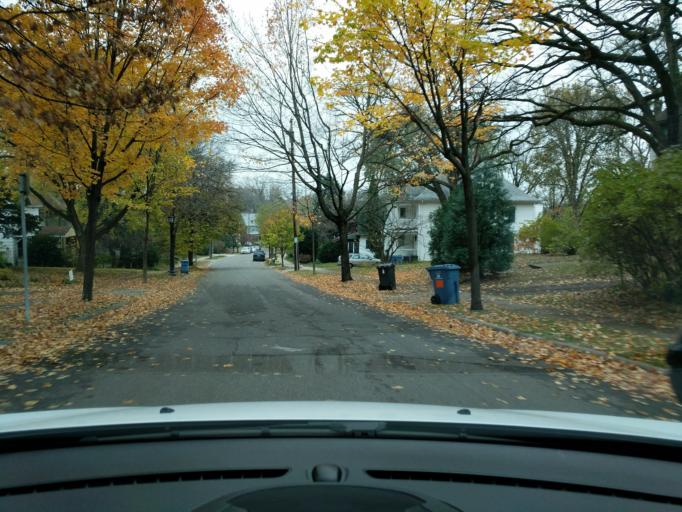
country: US
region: Minnesota
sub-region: Ramsey County
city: Lauderdale
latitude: 44.9675
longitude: -93.2110
